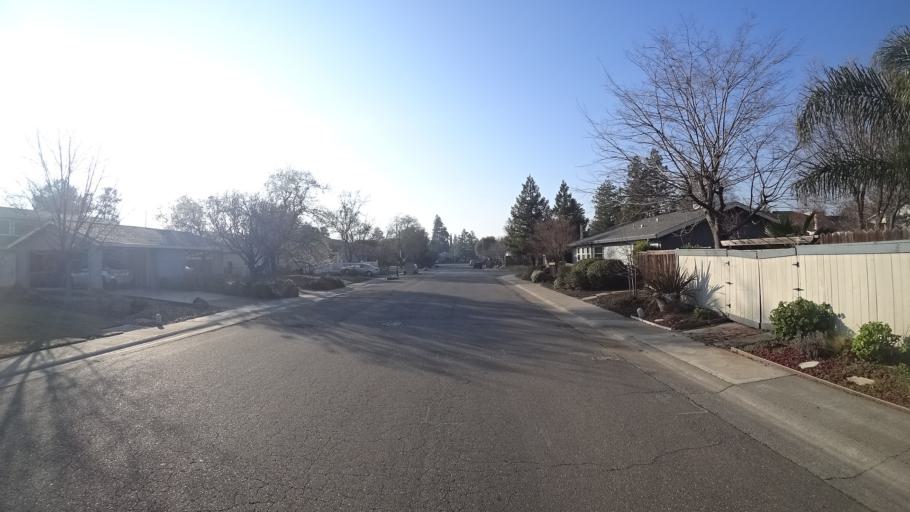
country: US
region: California
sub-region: Yolo County
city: Davis
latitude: 38.5594
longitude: -121.7908
